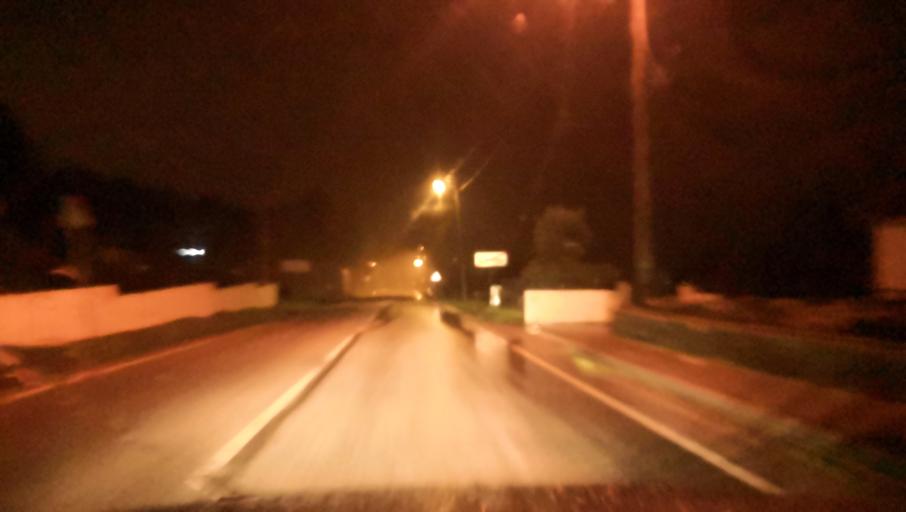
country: PT
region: Vila Real
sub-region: Vila Real
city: Vila Real
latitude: 41.3402
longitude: -7.7252
